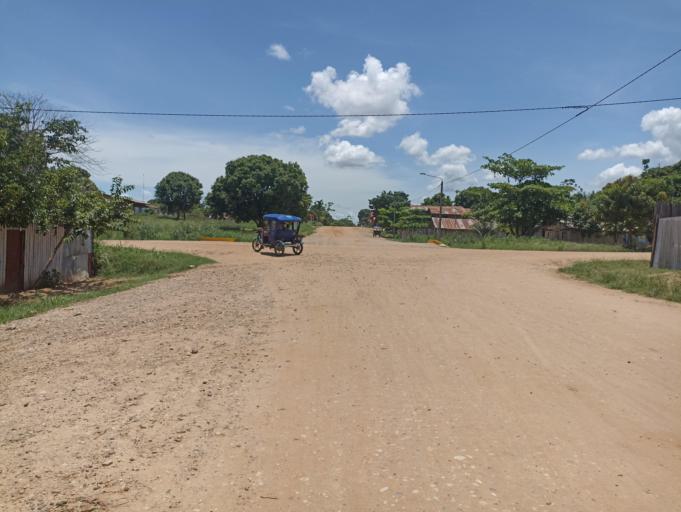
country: PE
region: Ucayali
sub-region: Provincia de Coronel Portillo
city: Puerto Callao
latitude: -8.3631
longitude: -74.5894
